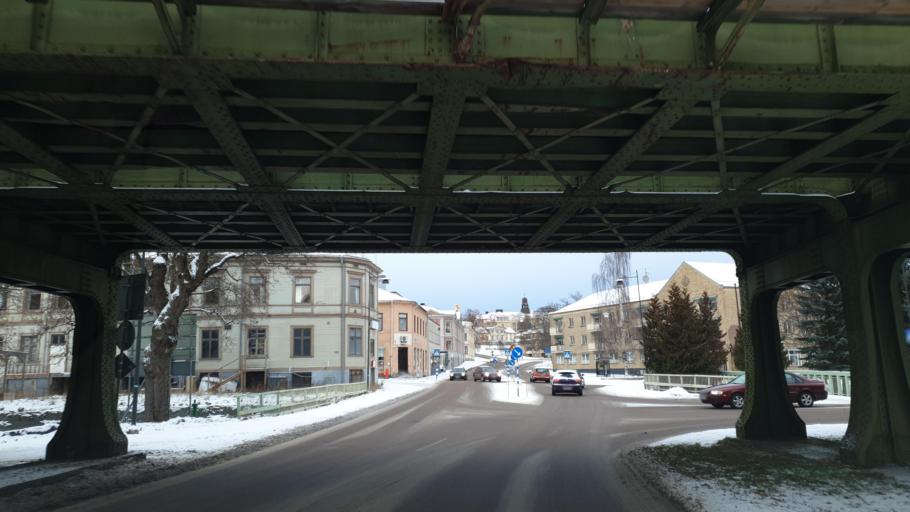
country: SE
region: Gaevleborg
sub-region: Soderhamns Kommun
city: Soderhamn
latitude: 61.3010
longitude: 17.0527
